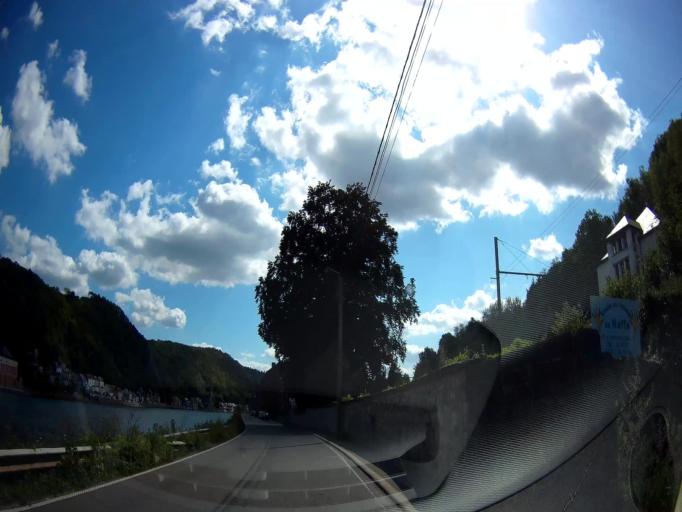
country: BE
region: Wallonia
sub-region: Province de Namur
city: Dinant
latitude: 50.2523
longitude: 4.9155
